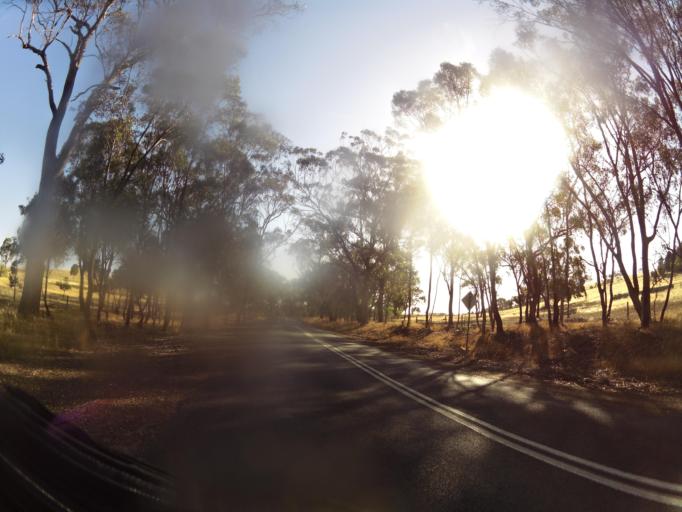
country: AU
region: Victoria
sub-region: Murrindindi
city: Kinglake West
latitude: -37.0093
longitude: 145.1235
